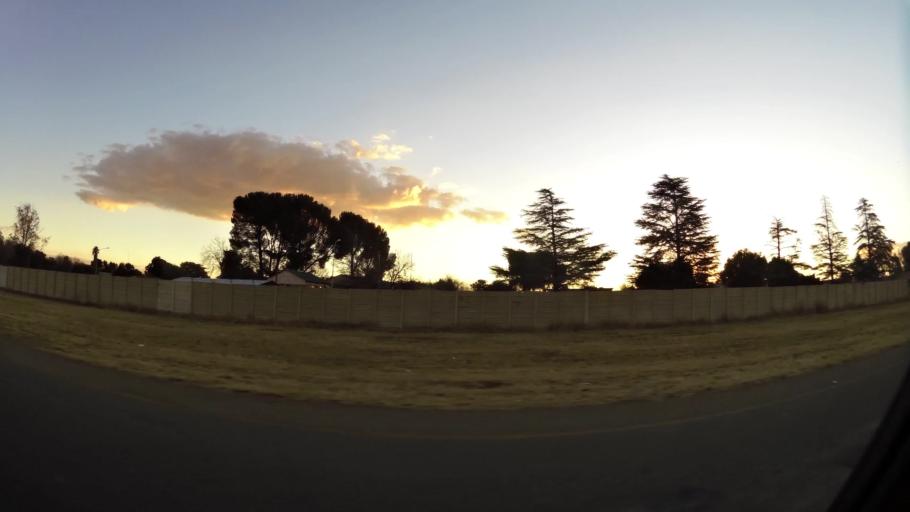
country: ZA
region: North-West
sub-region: Dr Kenneth Kaunda District Municipality
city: Potchefstroom
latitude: -26.6815
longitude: 27.0755
